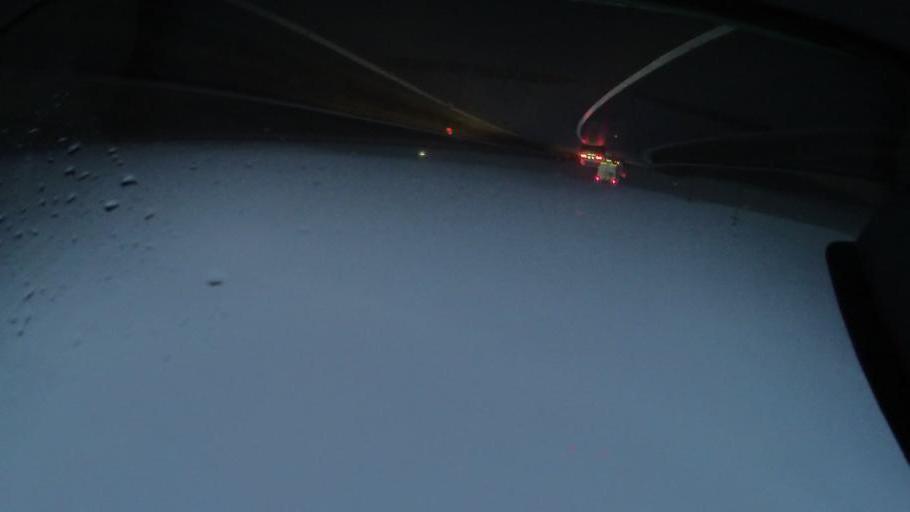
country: RO
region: Harghita
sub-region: Comuna Ditrau
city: Ditrau
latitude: 46.8242
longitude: 25.4923
